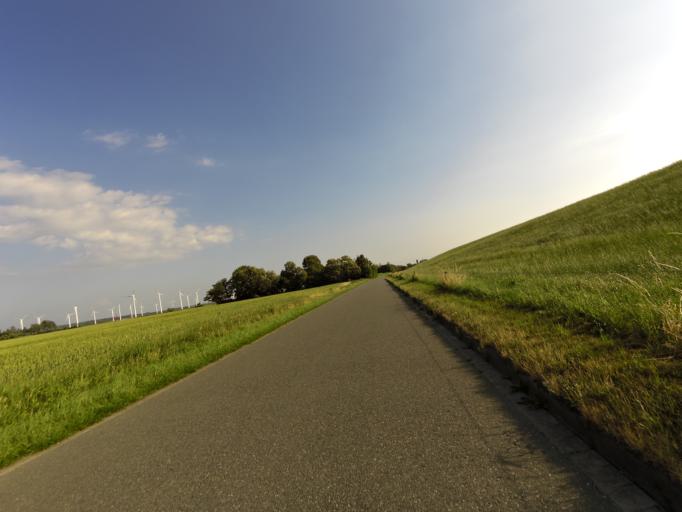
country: DE
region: Lower Saxony
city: Nordholz
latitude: 53.8052
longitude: 8.5699
